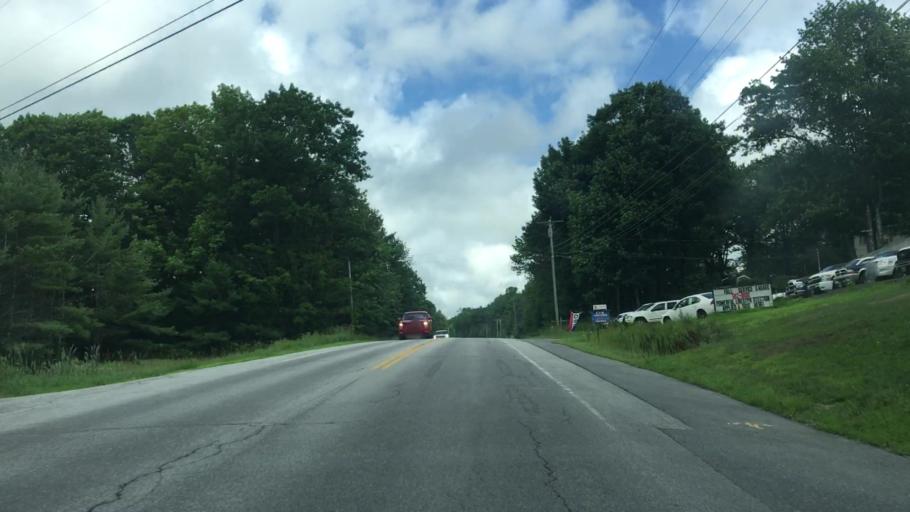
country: US
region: Maine
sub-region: Kennebec County
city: Farmingdale
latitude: 44.2602
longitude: -69.7647
